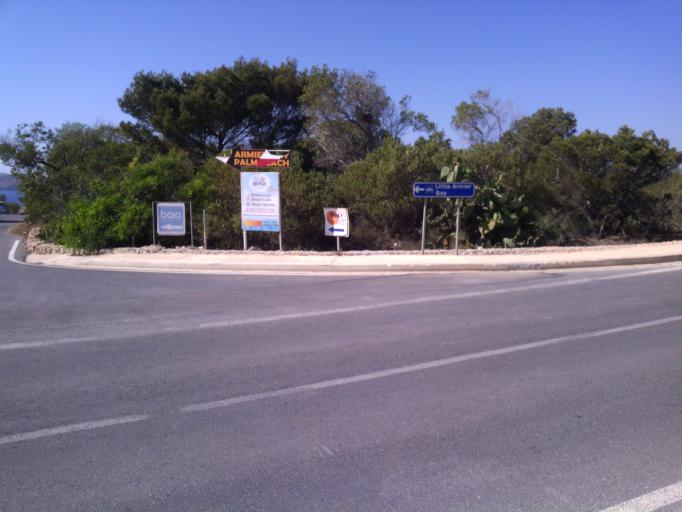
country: MT
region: Il-Mellieha
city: Mellieha
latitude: 35.9839
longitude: 14.3628
